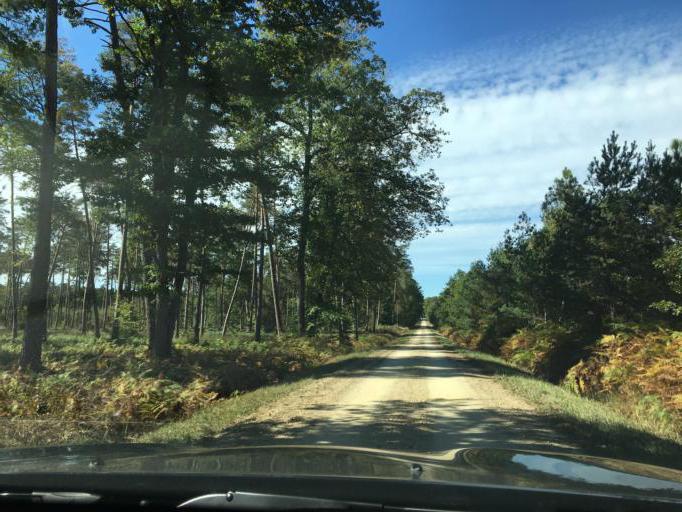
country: FR
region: Centre
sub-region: Departement d'Indre-et-Loire
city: Cheille
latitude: 47.2269
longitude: 0.4037
